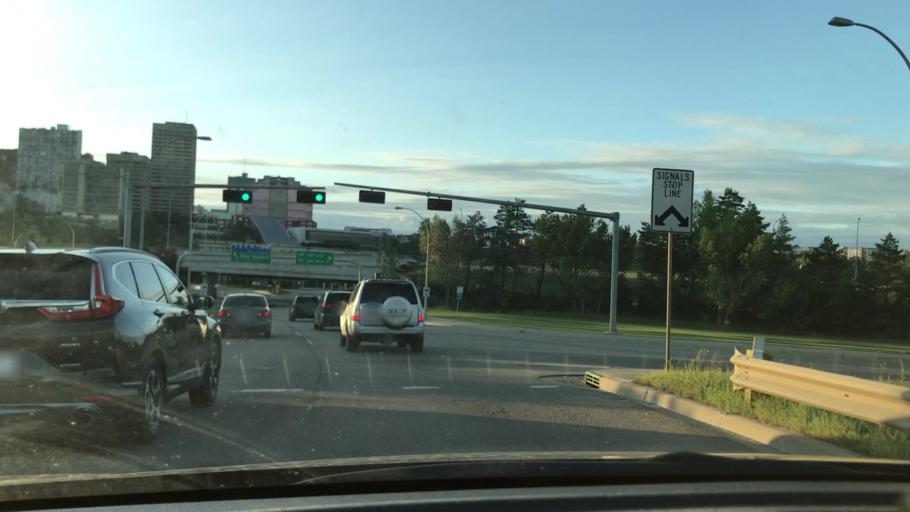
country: CA
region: Alberta
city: Edmonton
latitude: 53.5347
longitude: -113.4834
